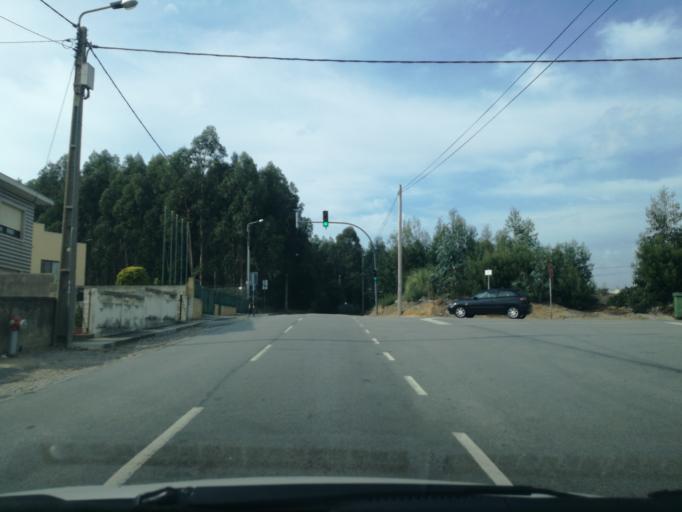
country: PT
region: Porto
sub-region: Vila Nova de Gaia
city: Sao Felix da Marinha
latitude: 41.0263
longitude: -8.6300
